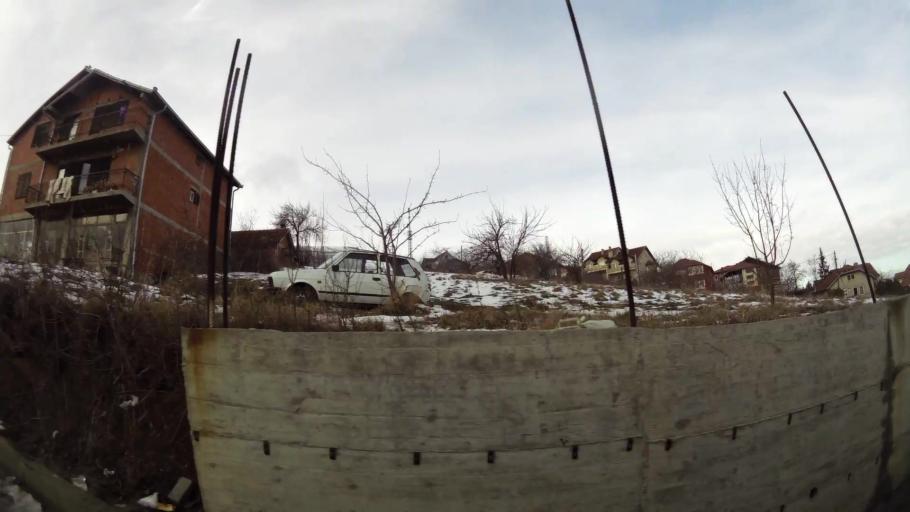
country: XK
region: Pristina
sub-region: Komuna e Prishtines
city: Pristina
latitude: 42.6717
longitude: 21.1837
